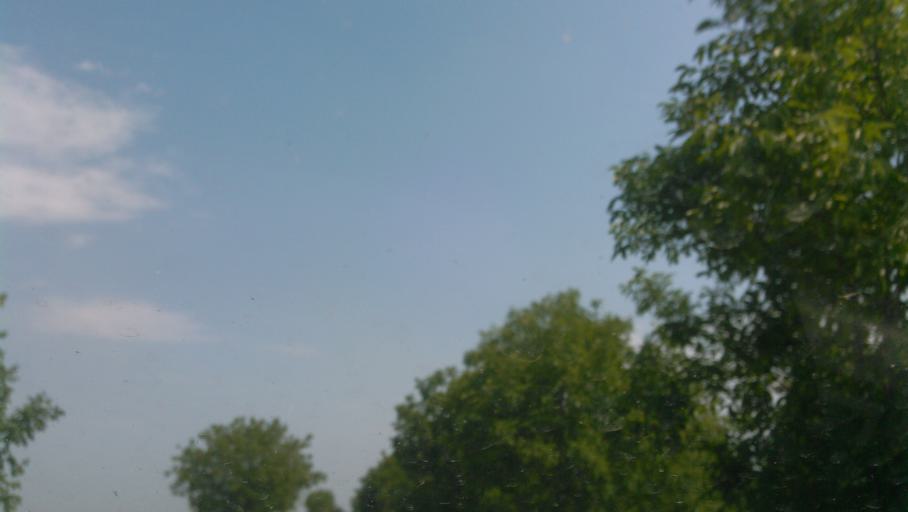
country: SK
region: Trnavsky
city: Dunajska Streda
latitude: 48.0461
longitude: 17.4891
